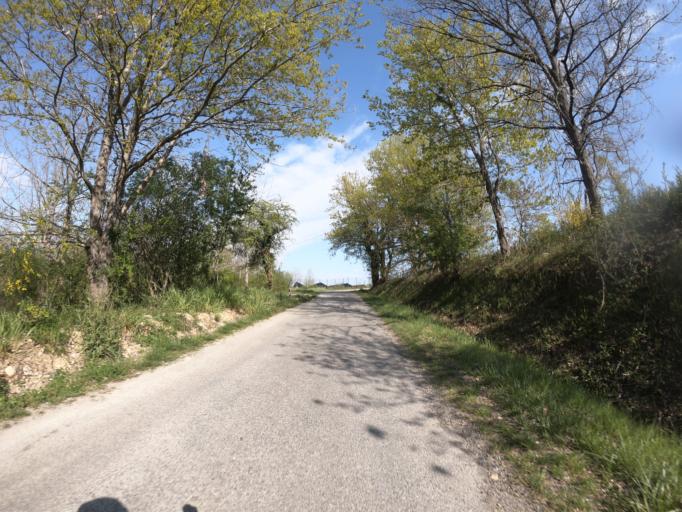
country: FR
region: Midi-Pyrenees
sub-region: Departement de l'Ariege
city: La Tour-du-Crieu
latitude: 43.1070
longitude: 1.6912
